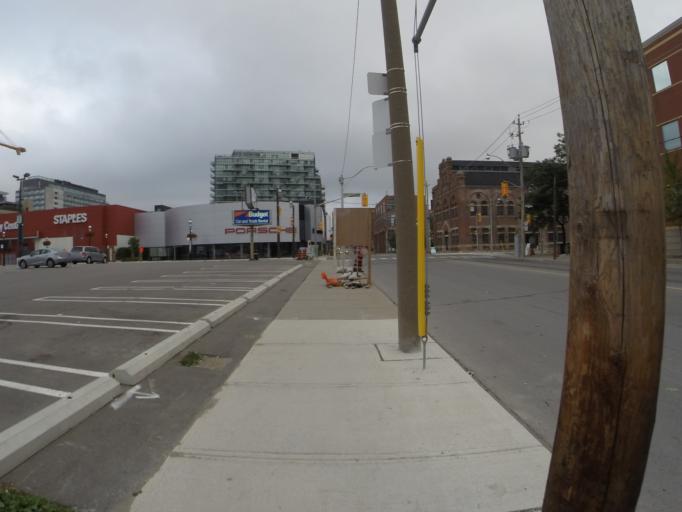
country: CA
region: Ontario
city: Toronto
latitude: 43.6506
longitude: -79.3635
